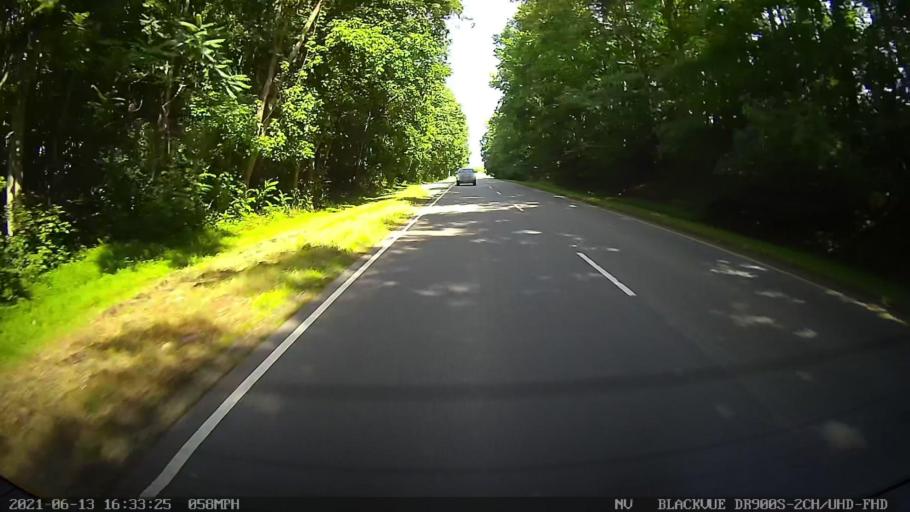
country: US
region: Virginia
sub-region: City of Hopewell
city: Hopewell
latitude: 37.2861
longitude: -77.2483
